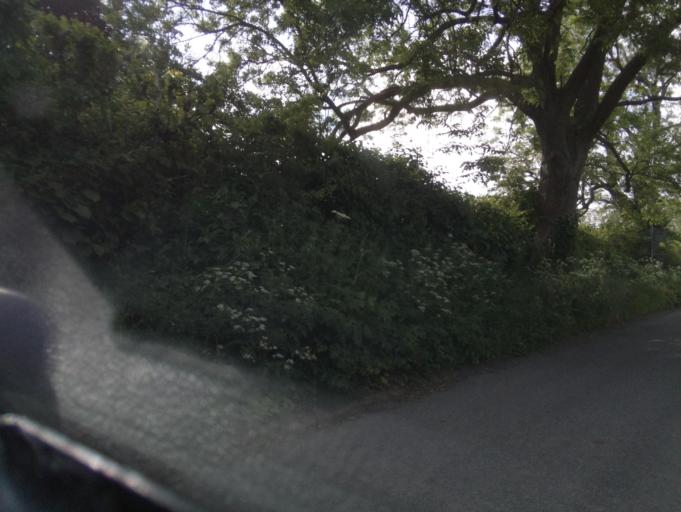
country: GB
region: England
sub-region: Gloucestershire
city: Chipping Campden
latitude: 52.0522
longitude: -1.8012
